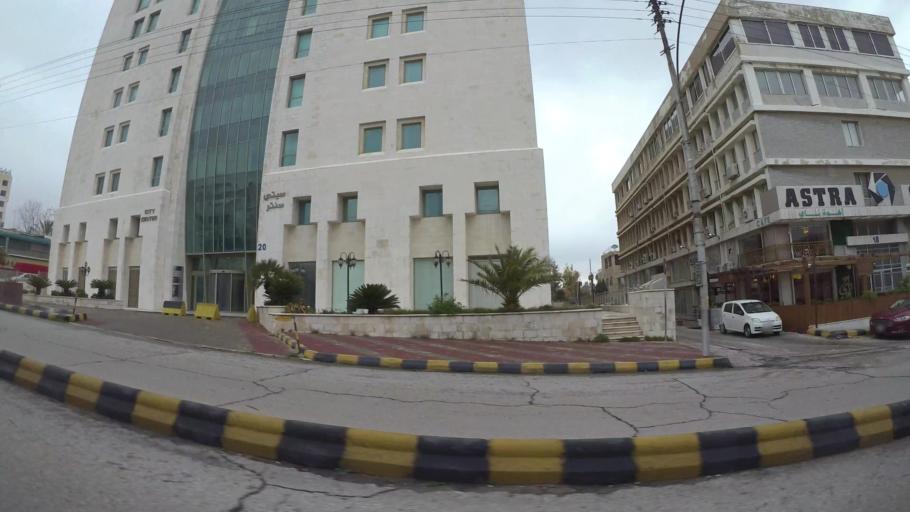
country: JO
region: Amman
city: Amman
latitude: 31.9507
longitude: 35.9196
